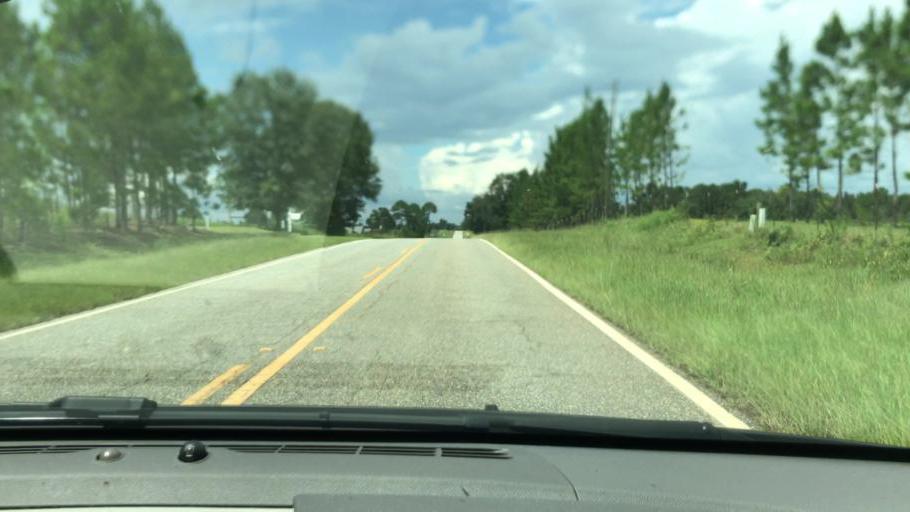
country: US
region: Georgia
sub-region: Early County
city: Blakely
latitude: 31.2714
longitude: -84.9906
